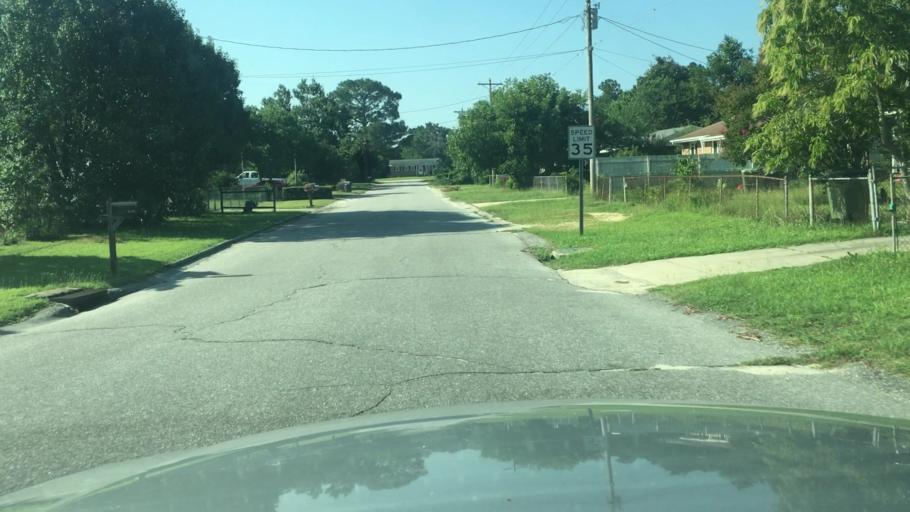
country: US
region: North Carolina
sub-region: Cumberland County
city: Spring Lake
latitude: 35.1534
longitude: -78.9196
